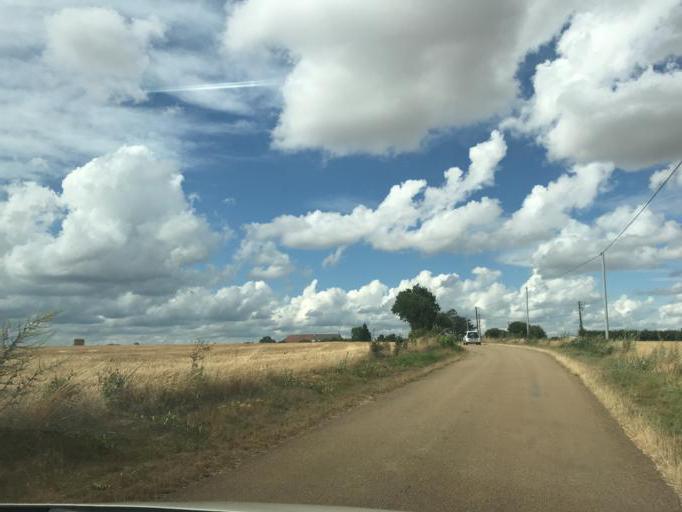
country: FR
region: Bourgogne
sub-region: Departement de l'Yonne
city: Fontenailles
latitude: 47.5713
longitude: 3.3443
